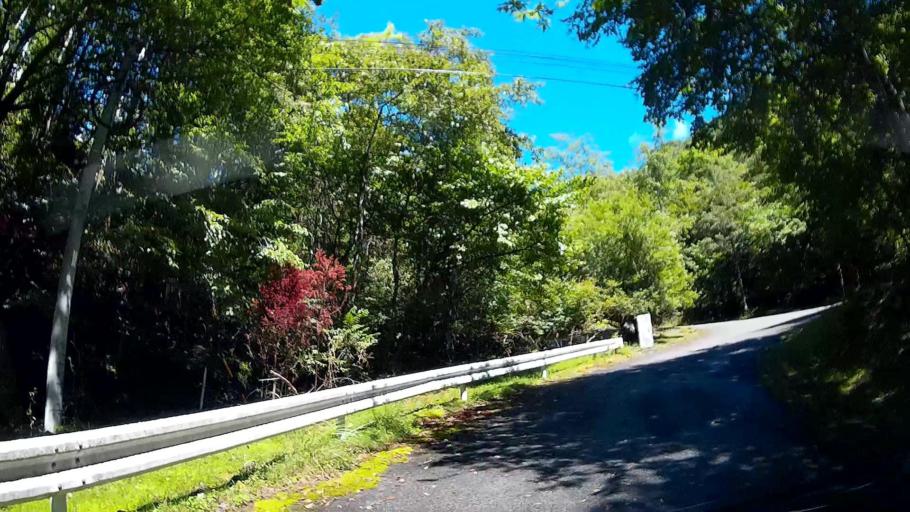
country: JP
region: Shizuoka
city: Fujinomiya
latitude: 35.2932
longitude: 138.3158
